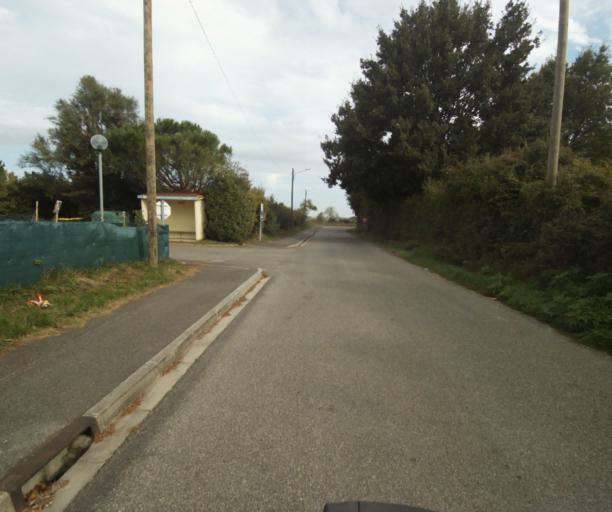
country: FR
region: Midi-Pyrenees
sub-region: Departement du Tarn-et-Garonne
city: Finhan
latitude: 43.9199
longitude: 1.2227
